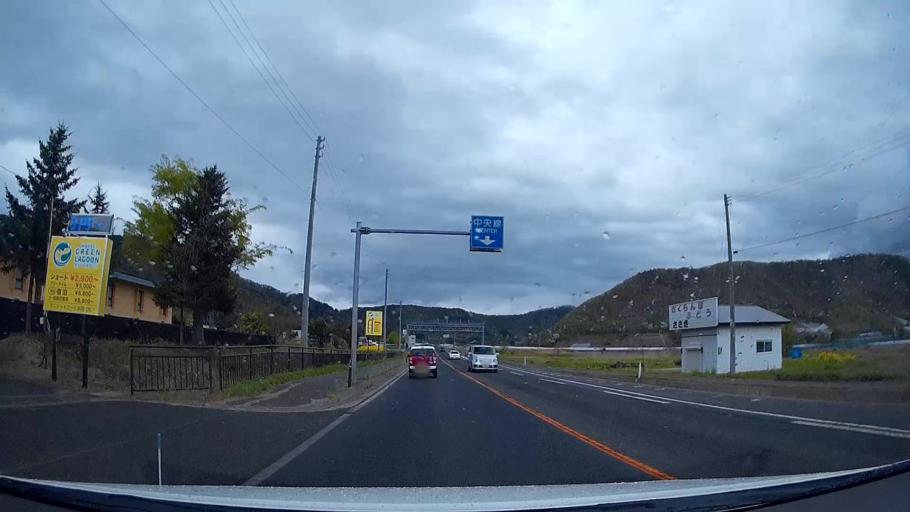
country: JP
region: Yamagata
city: Takahata
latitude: 38.0789
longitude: 140.1847
